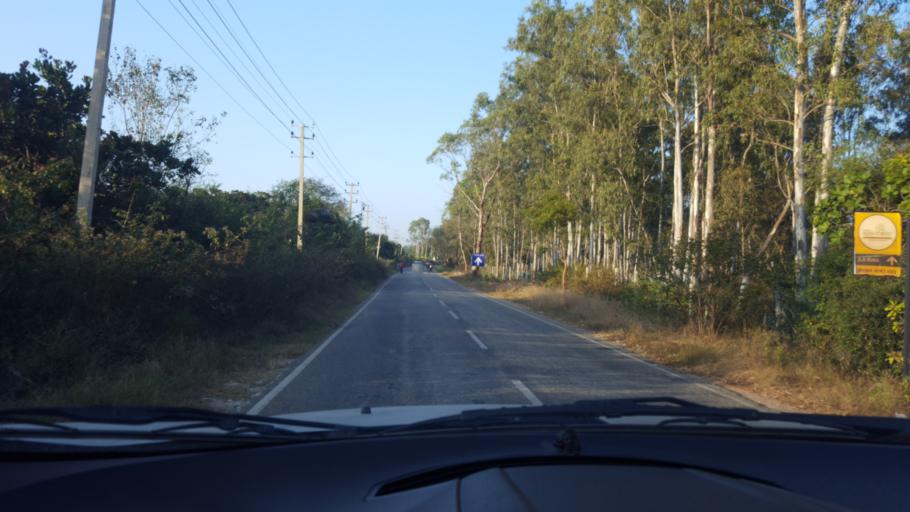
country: IN
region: Karnataka
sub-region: Bangalore Urban
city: Yelahanka
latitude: 13.1821
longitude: 77.5994
